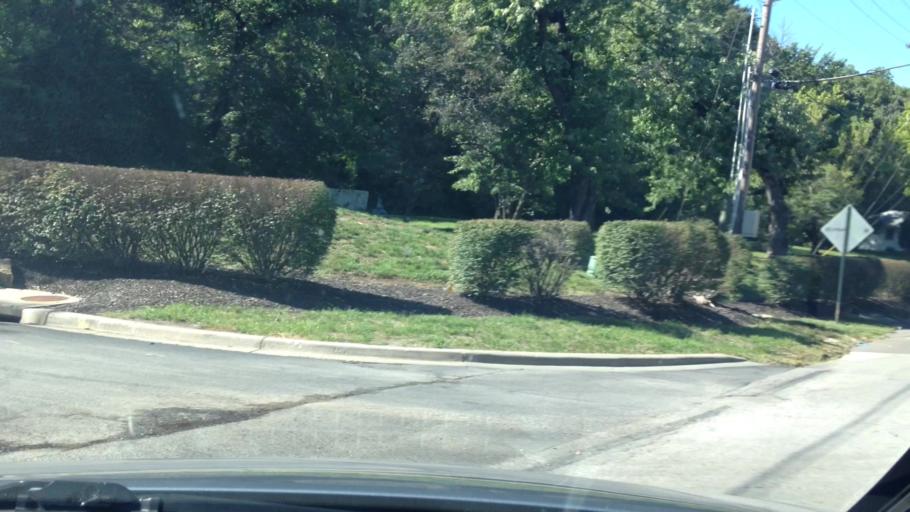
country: US
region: Kansas
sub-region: Johnson County
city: Roeland Park
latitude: 39.0448
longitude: -94.6399
